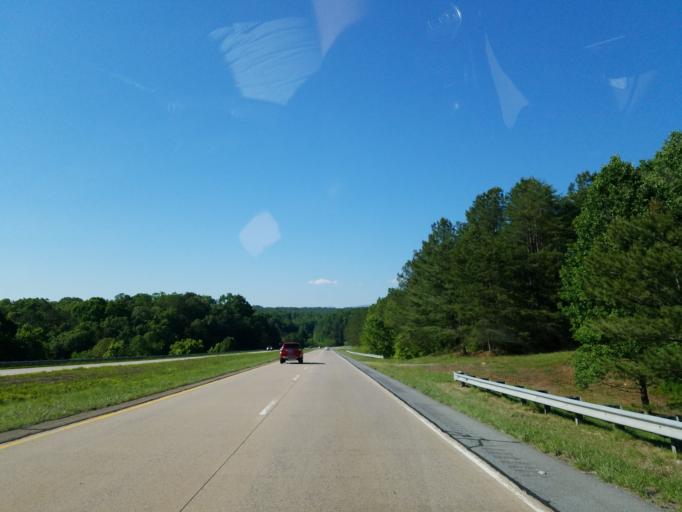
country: US
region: Georgia
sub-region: Gilmer County
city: Ellijay
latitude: 34.6140
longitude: -84.5178
